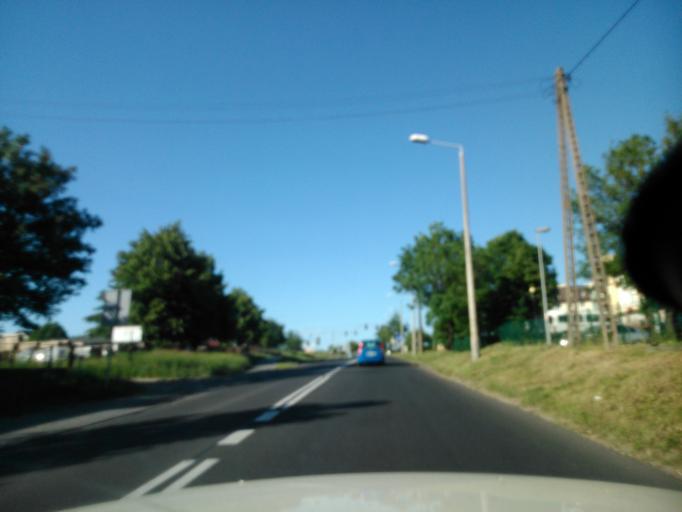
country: PL
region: Kujawsko-Pomorskie
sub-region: Powiat torunski
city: Lubicz Dolny
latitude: 53.0514
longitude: 18.7078
